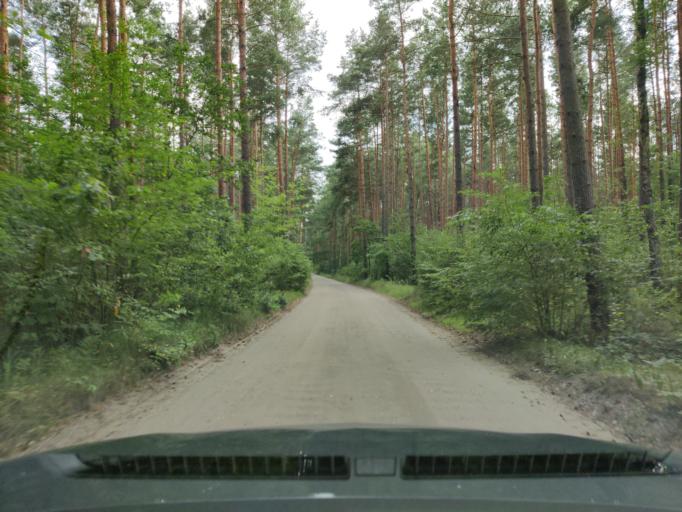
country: PL
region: Masovian Voivodeship
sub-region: Powiat pultuski
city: Pultusk
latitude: 52.7516
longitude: 21.1412
